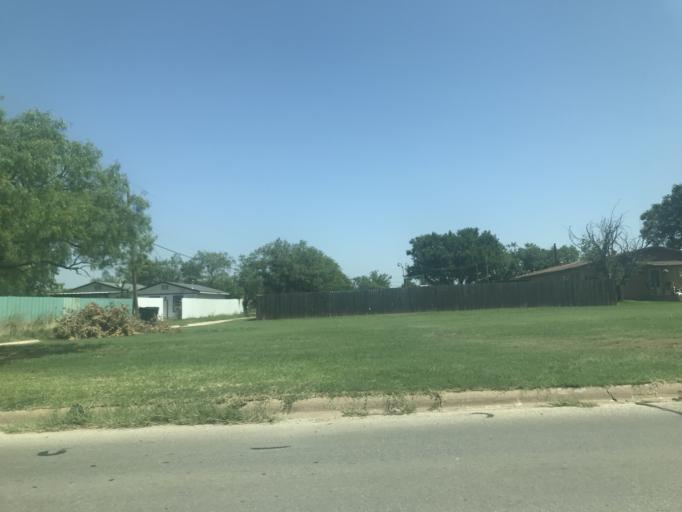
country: US
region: Texas
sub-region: Taylor County
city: Abilene
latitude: 32.4700
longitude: -99.7437
